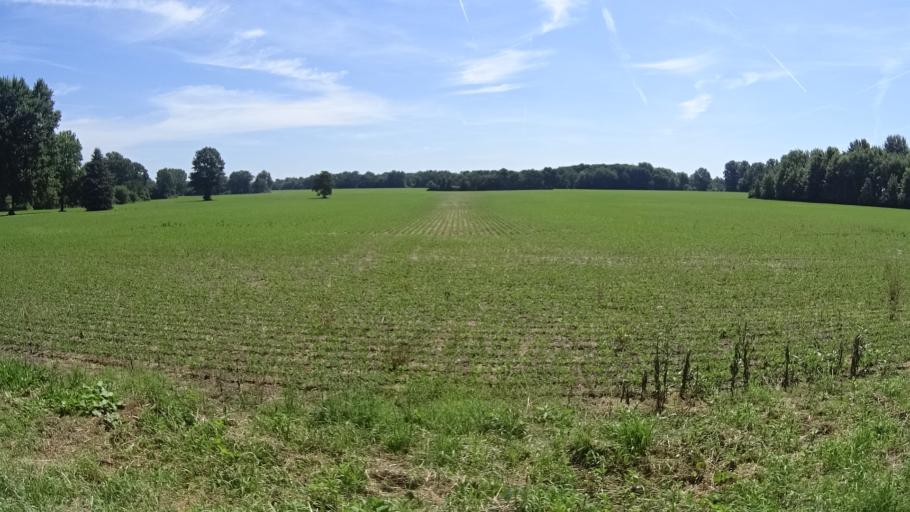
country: US
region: Ohio
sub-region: Erie County
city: Huron
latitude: 41.3496
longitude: -82.4592
